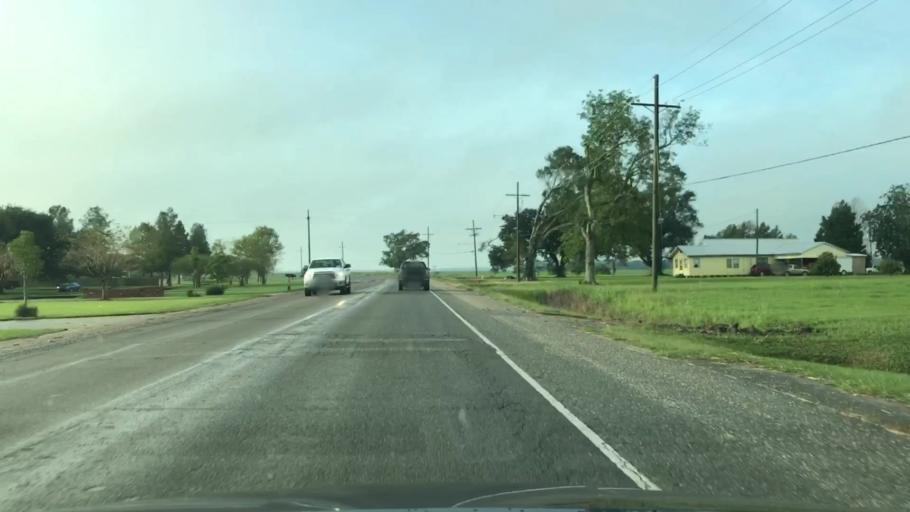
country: US
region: Louisiana
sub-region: Terrebonne Parish
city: Gray
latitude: 29.6646
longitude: -90.8196
